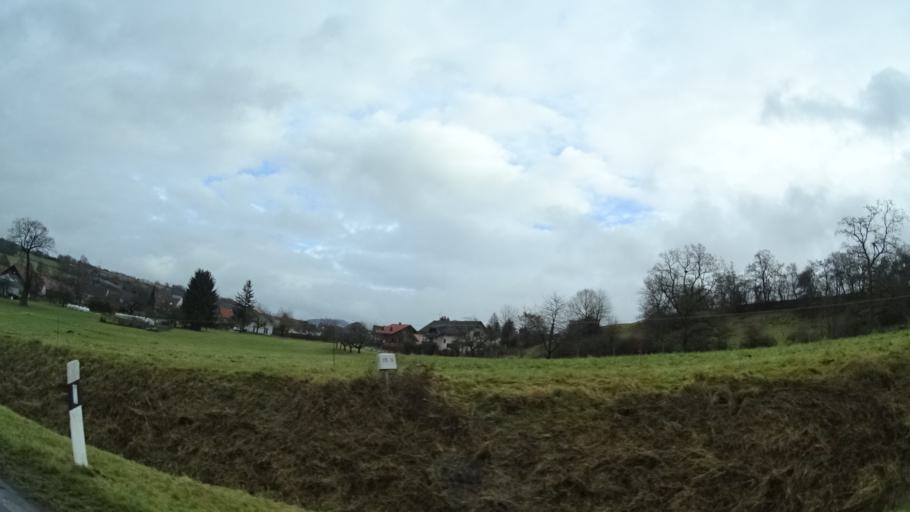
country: DE
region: Hesse
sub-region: Regierungsbezirk Giessen
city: Schotten
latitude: 50.5730
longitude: 9.1189
